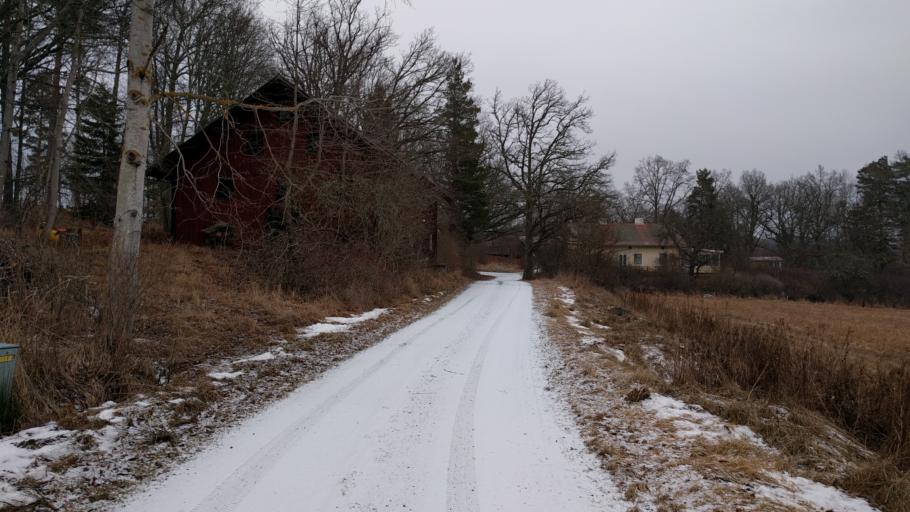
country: SE
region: OEstergoetland
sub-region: Valdemarsviks Kommun
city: Gusum
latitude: 58.4639
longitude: 16.6021
